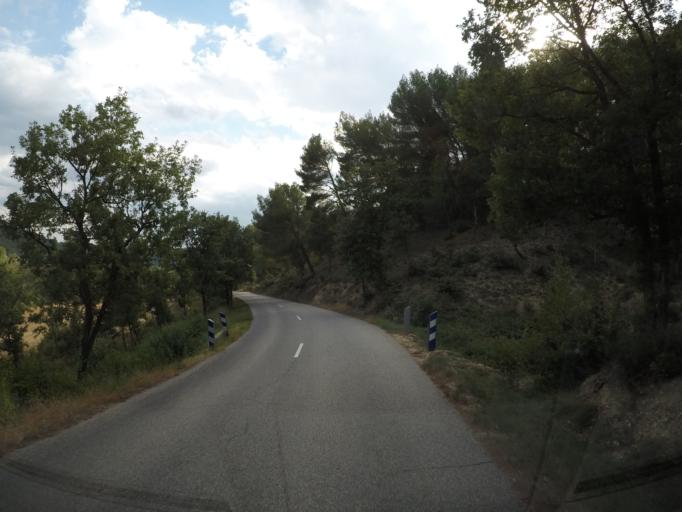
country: FR
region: Provence-Alpes-Cote d'Azur
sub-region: Departement des Alpes-de-Haute-Provence
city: Riez
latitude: 43.8238
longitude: 6.0539
